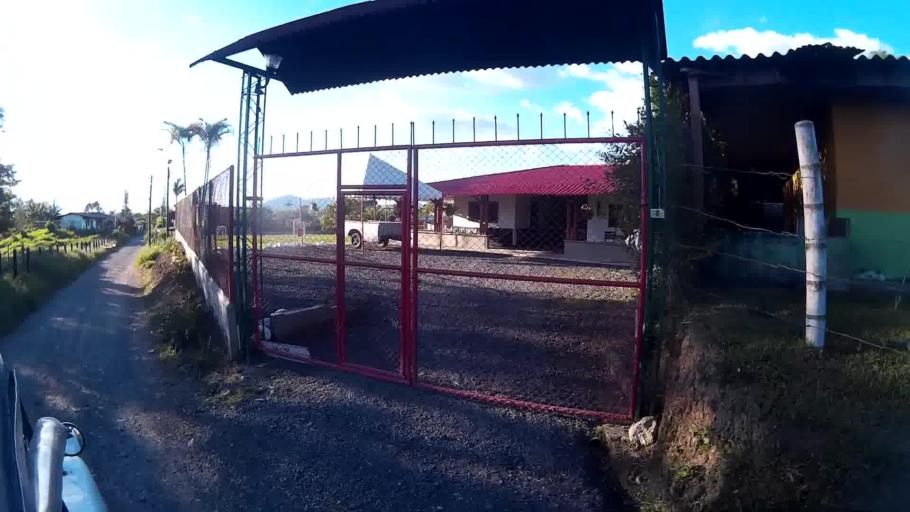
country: CO
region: Quindio
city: Filandia
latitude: 4.7215
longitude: -75.6784
